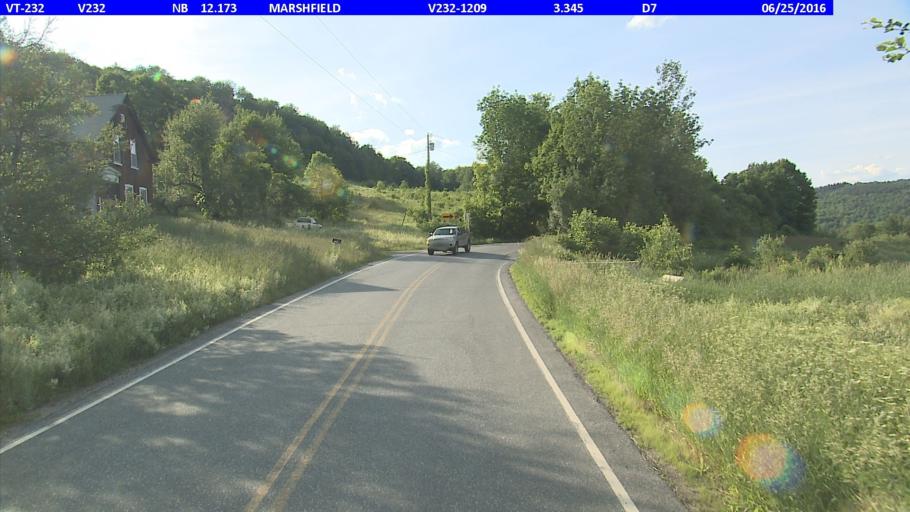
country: US
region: Vermont
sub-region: Caledonia County
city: Hardwick
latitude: 44.3529
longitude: -72.3059
